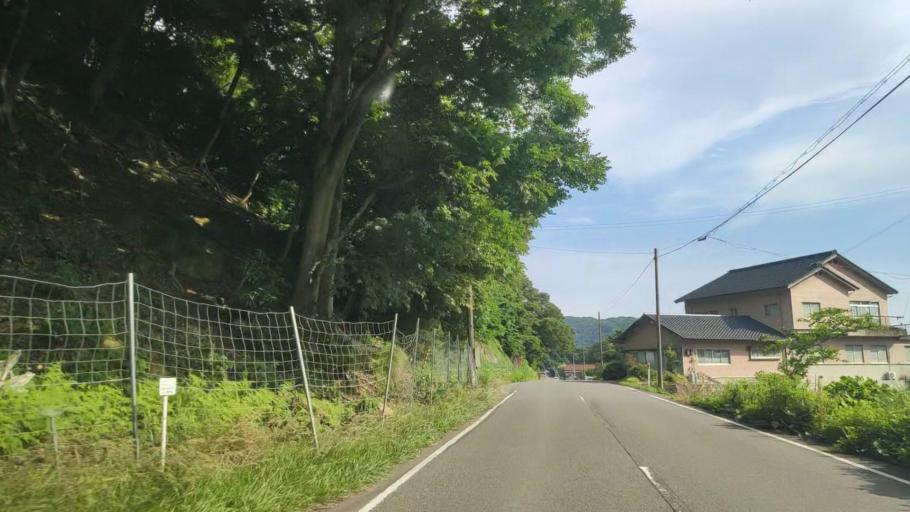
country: JP
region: Hyogo
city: Toyooka
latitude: 35.6353
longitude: 134.8367
